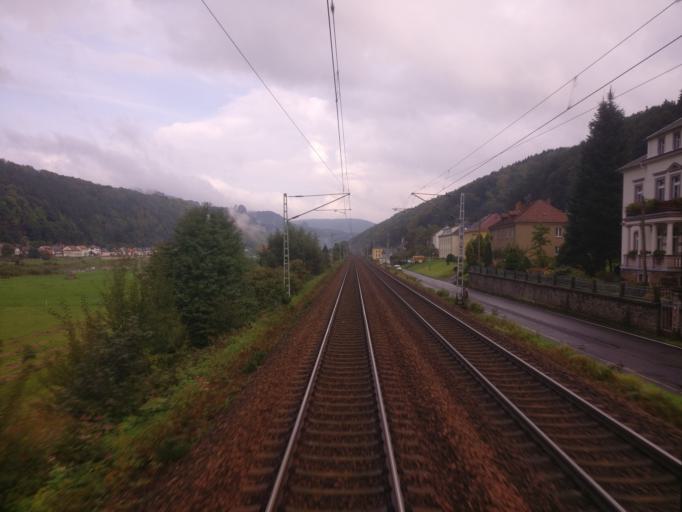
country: DE
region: Saxony
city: Bad Schandau
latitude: 50.9125
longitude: 14.1632
